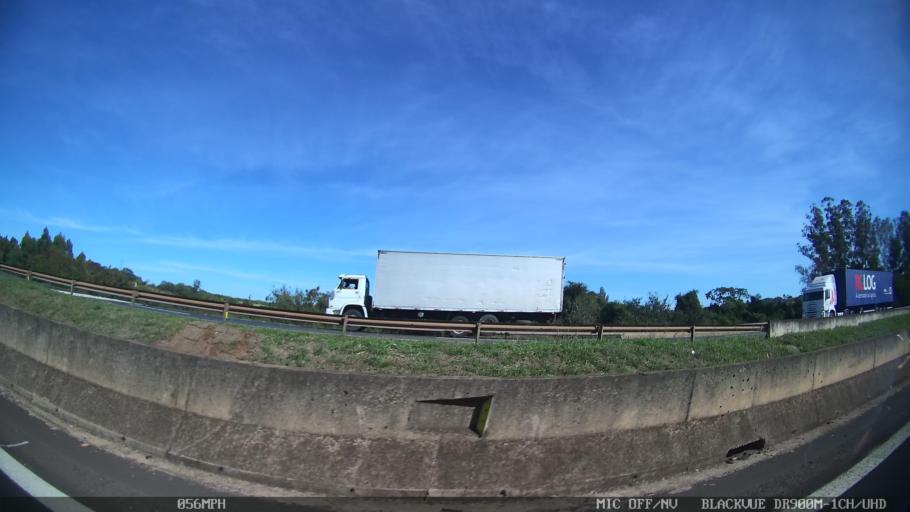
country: BR
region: Sao Paulo
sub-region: Leme
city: Leme
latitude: -22.0995
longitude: -47.4154
